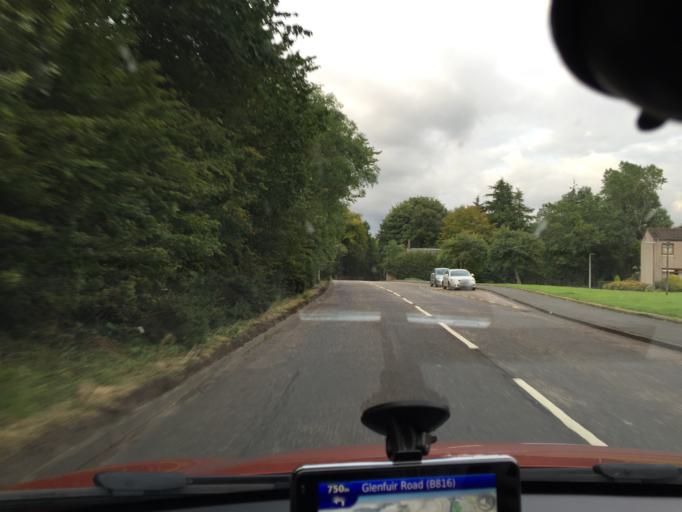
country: GB
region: Scotland
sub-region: Falkirk
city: Larbert
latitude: 55.9980
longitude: -3.8296
